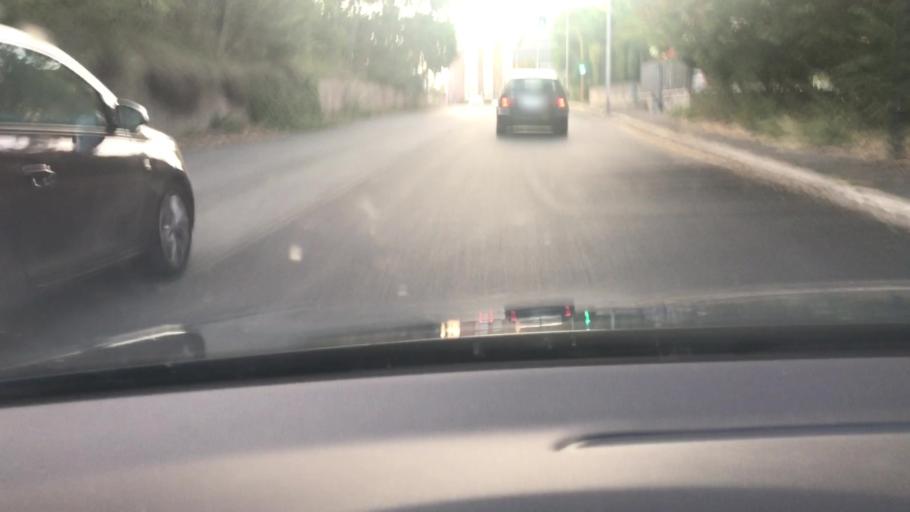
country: IT
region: Latium
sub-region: Citta metropolitana di Roma Capitale
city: Rome
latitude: 41.9291
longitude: 12.5629
